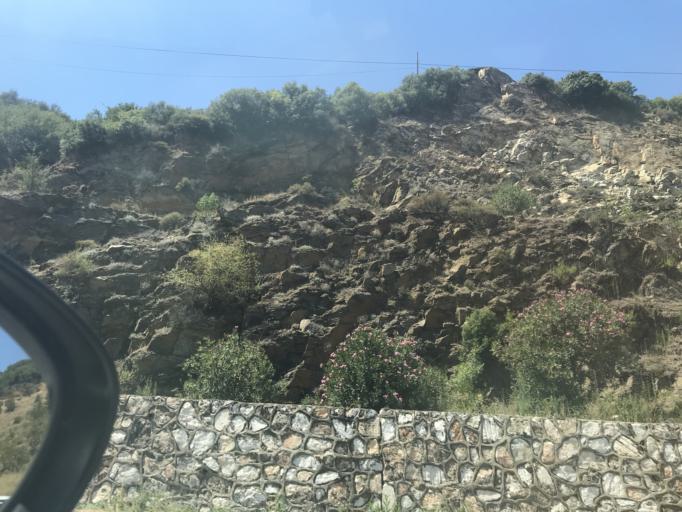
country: TR
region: Aydin
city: Akcaova
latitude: 37.5033
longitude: 28.1032
